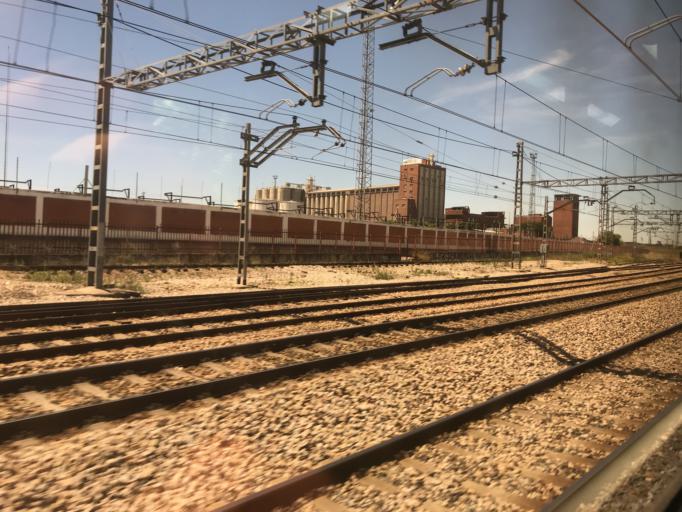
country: ES
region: Madrid
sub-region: Provincia de Madrid
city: Villaverde
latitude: 40.3326
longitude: -3.6940
